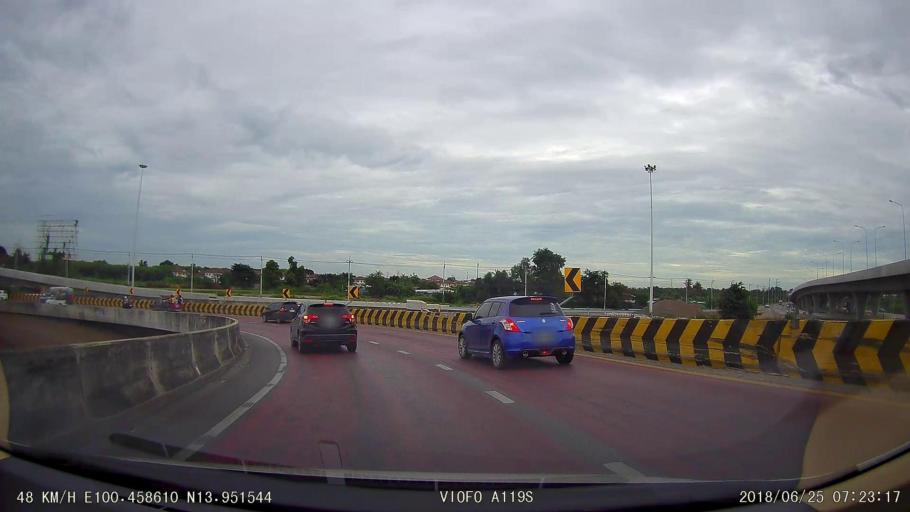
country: TH
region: Nonthaburi
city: Bang Bua Thong
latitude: 13.9515
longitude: 100.4584
